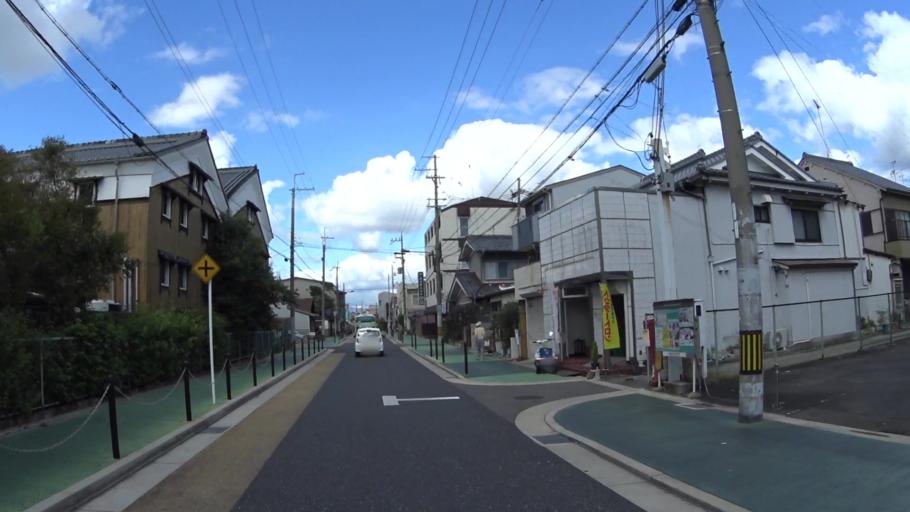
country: JP
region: Kyoto
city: Muko
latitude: 34.9402
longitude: 135.7571
